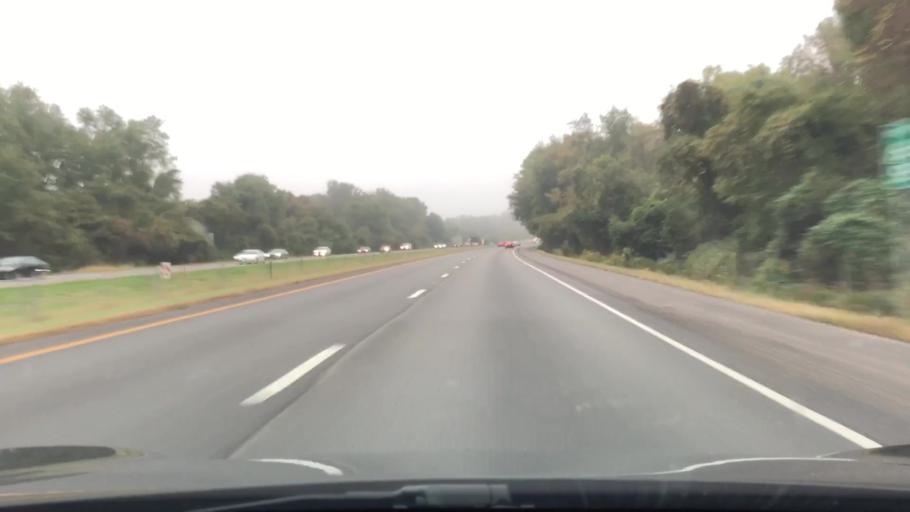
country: US
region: Pennsylvania
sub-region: Bucks County
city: Woodside
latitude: 40.2136
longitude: -74.8773
